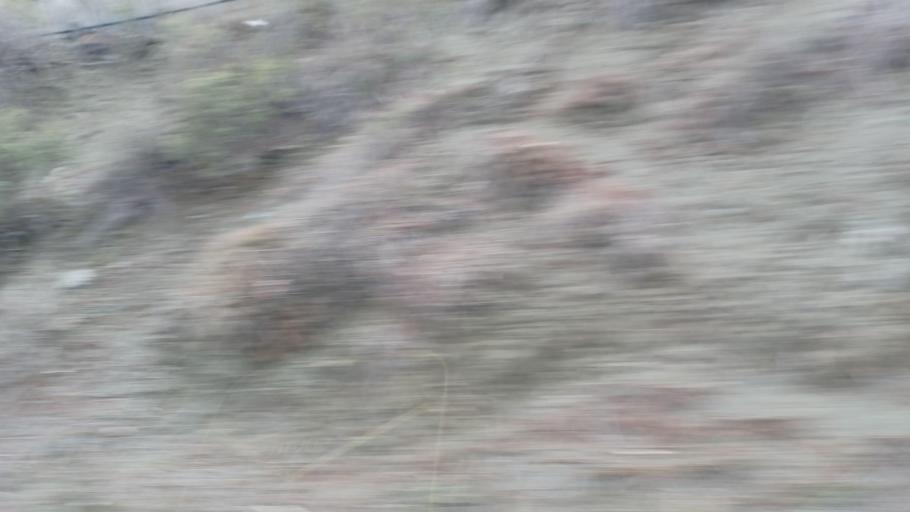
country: CY
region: Limassol
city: Kyperounta
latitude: 34.9359
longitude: 32.9773
